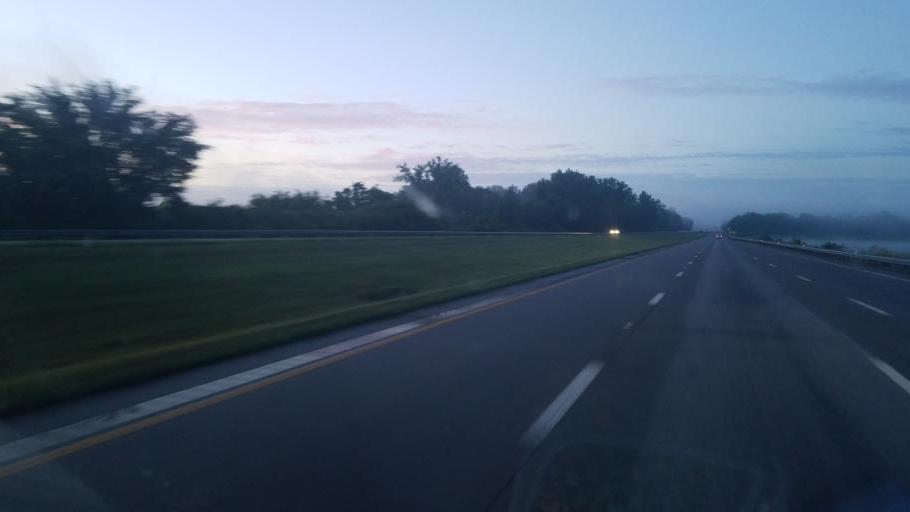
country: US
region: Ohio
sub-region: Ross County
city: Chillicothe
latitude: 39.3126
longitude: -82.9279
